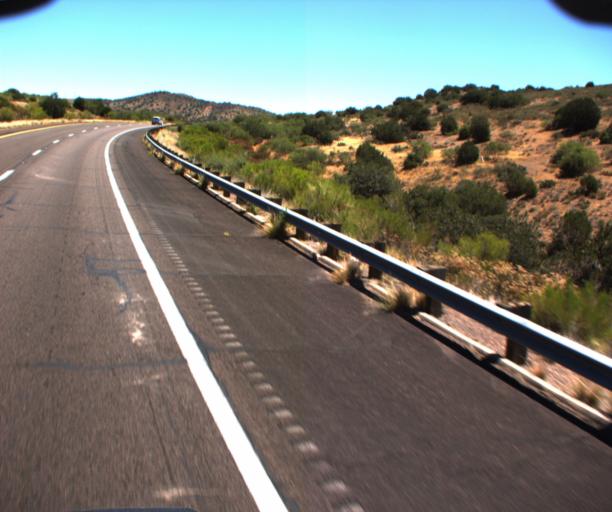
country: US
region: Arizona
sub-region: Gila County
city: Tonto Basin
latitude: 33.9627
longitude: -111.3910
